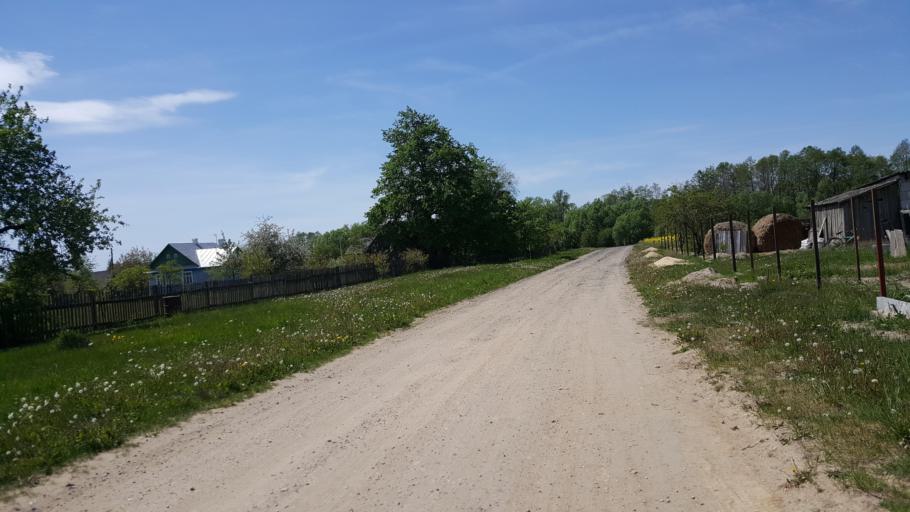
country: BY
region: Brest
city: Kobryn
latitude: 52.3421
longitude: 24.2433
